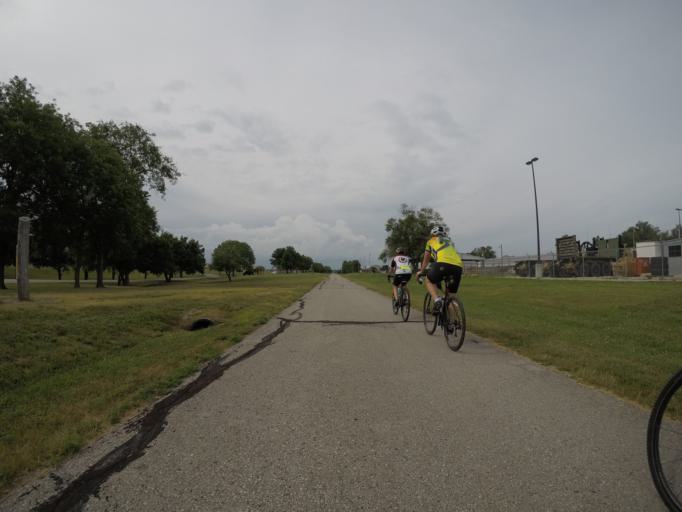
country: US
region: Kansas
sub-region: Franklin County
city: Ottawa
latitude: 38.5895
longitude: -95.2705
